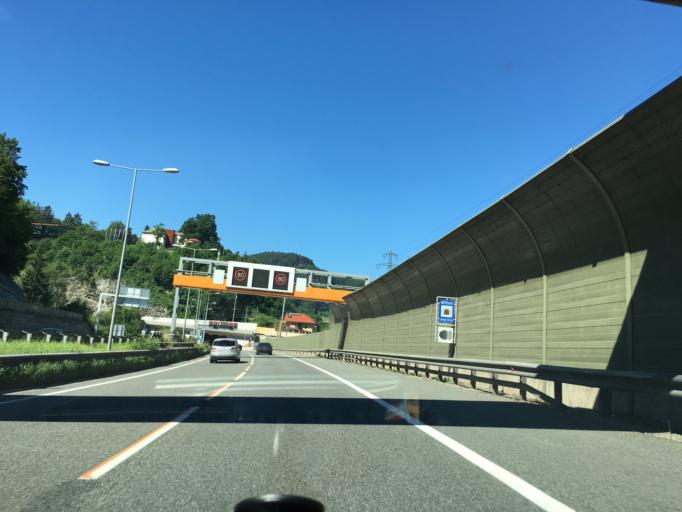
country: AT
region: Tyrol
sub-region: Innsbruck Stadt
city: Innsbruck
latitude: 47.2528
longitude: 11.4051
